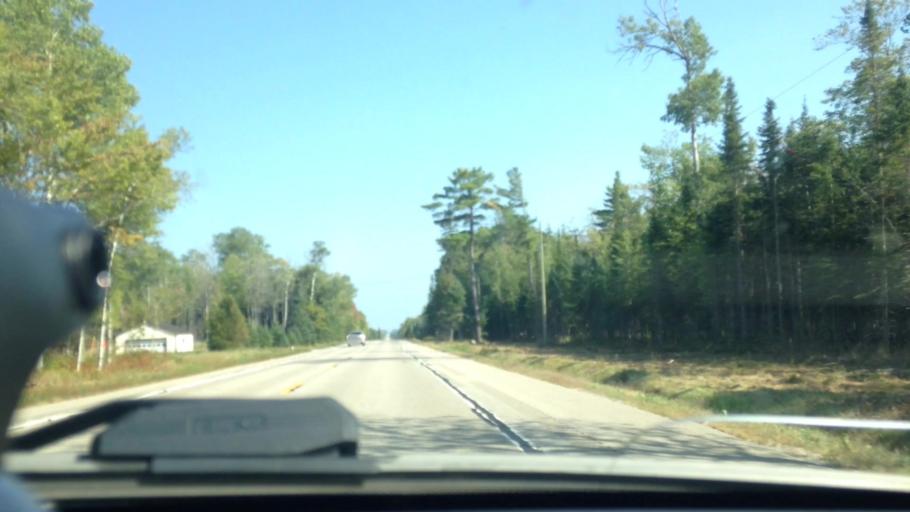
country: US
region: Michigan
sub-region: Luce County
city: Newberry
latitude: 46.3034
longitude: -85.3562
